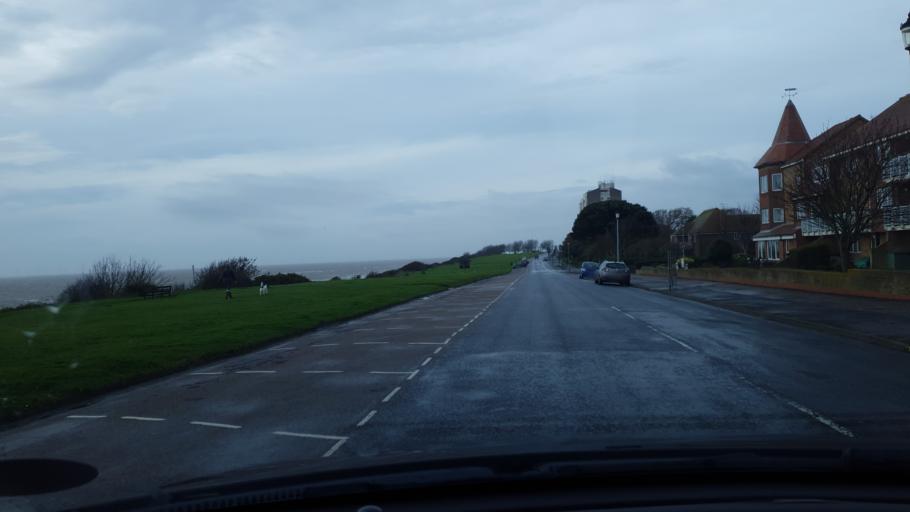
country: GB
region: England
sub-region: Essex
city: Frinton-on-Sea
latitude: 51.8338
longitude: 1.2527
